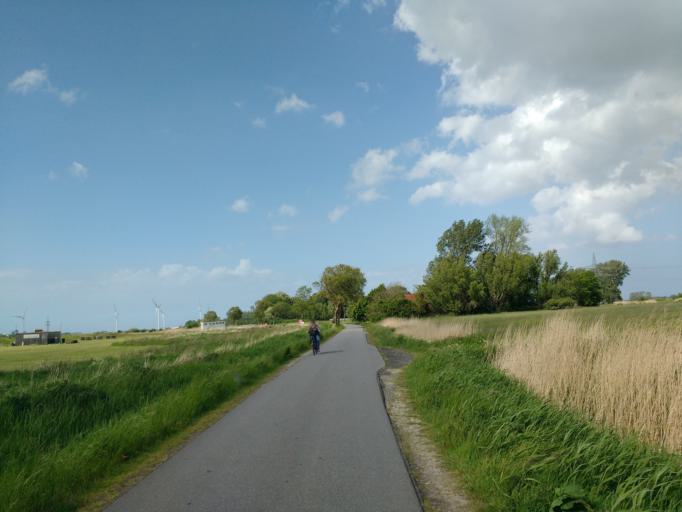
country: DE
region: Lower Saxony
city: Schillig
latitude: 53.6699
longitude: 7.9294
